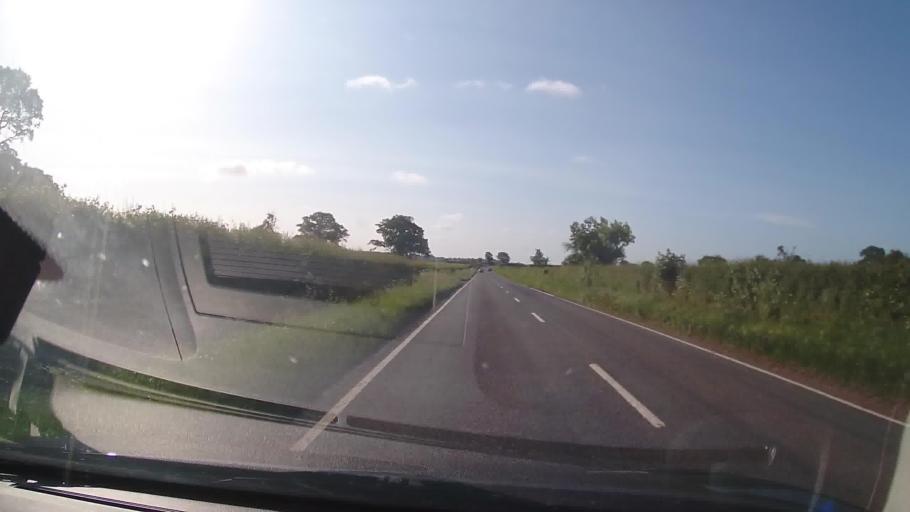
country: GB
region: England
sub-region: Shropshire
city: Wem
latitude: 52.8373
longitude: -2.7040
